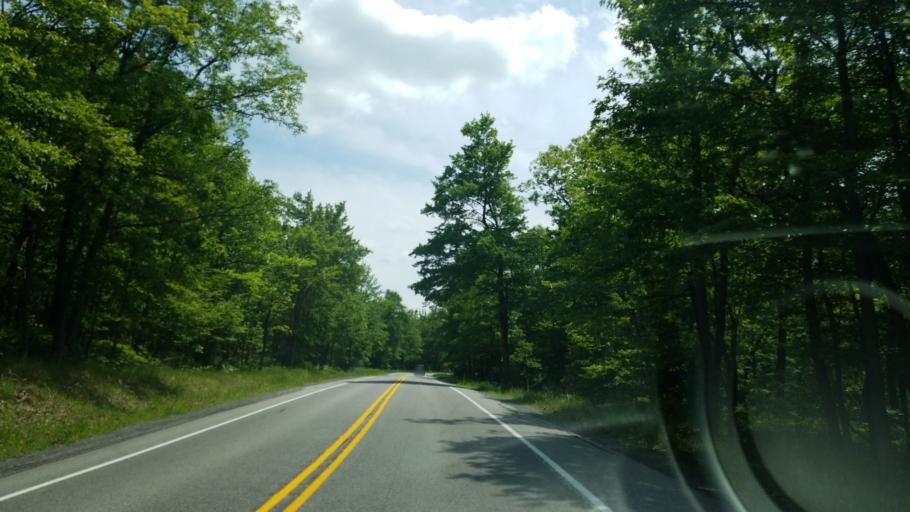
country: US
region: Pennsylvania
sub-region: Blair County
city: Tyrone
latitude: 40.7032
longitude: -78.2963
